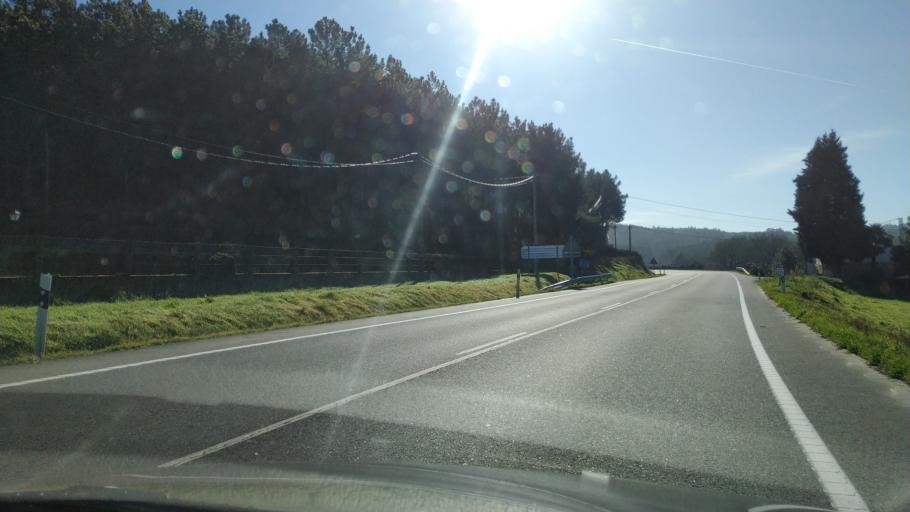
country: ES
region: Galicia
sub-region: Provincia da Coruna
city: Ribeira
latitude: 42.7540
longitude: -8.3541
